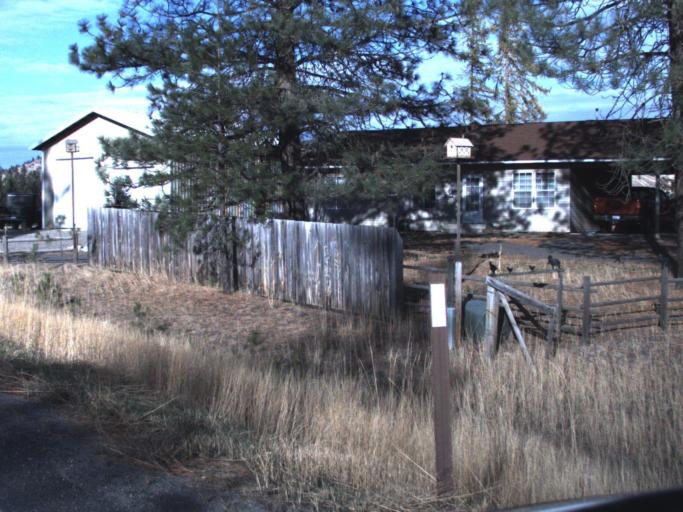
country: US
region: Washington
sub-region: Stevens County
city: Kettle Falls
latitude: 48.5856
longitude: -118.0736
